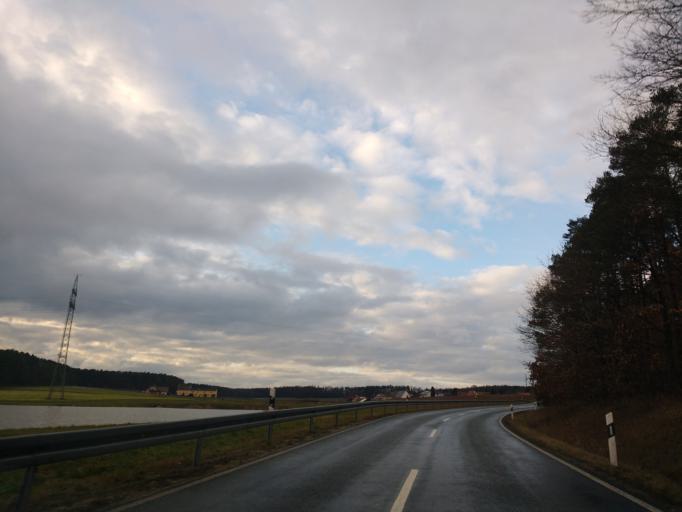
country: DE
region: Bavaria
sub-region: Regierungsbezirk Mittelfranken
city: Weisendorf
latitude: 49.6063
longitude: 10.8377
